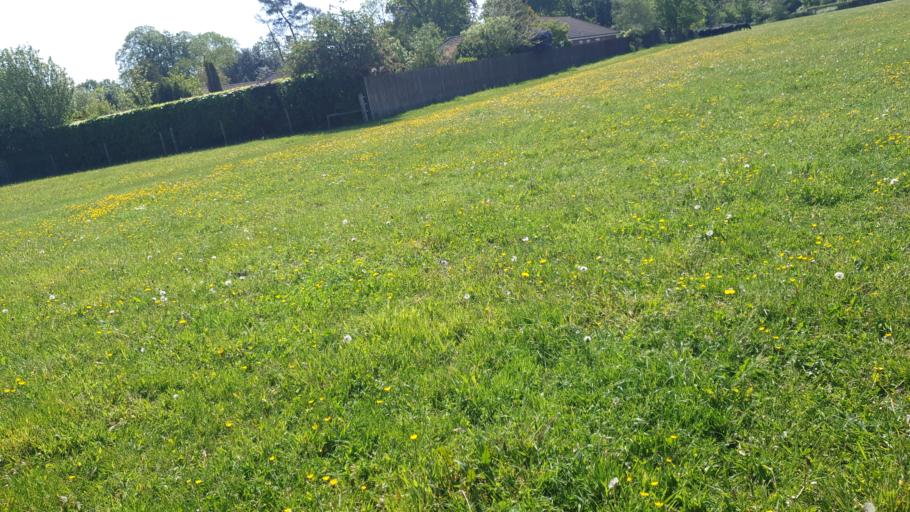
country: GB
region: England
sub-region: Essex
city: Manningtree
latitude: 51.9356
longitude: 1.0399
